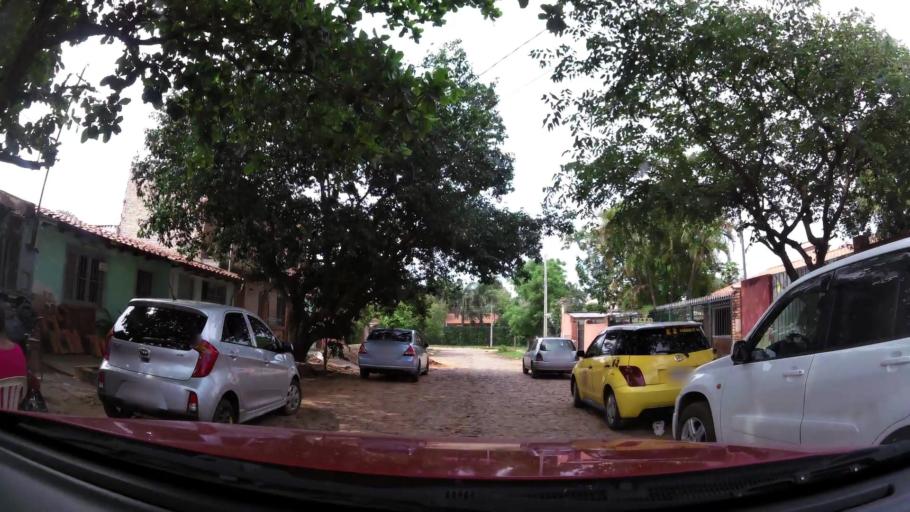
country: PY
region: Central
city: Fernando de la Mora
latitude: -25.2711
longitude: -57.5575
